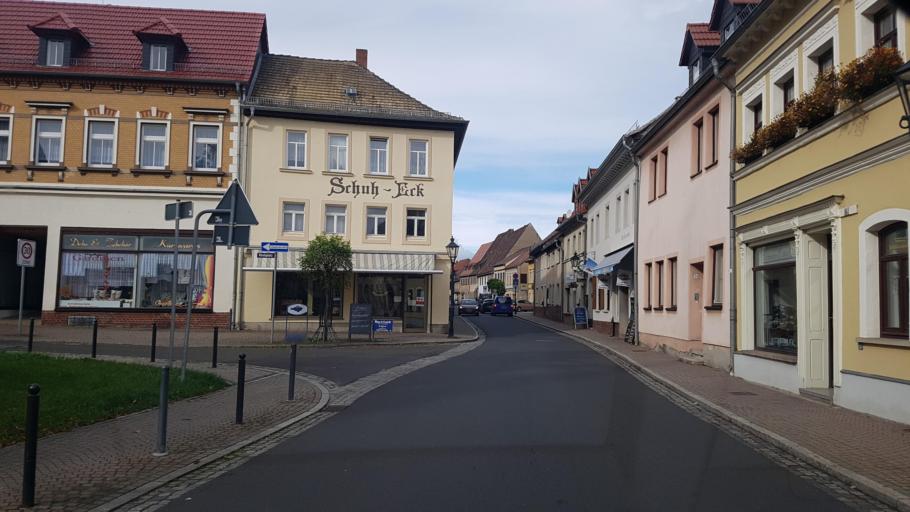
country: DE
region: Saxony
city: Pegau
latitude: 51.1673
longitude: 12.2531
